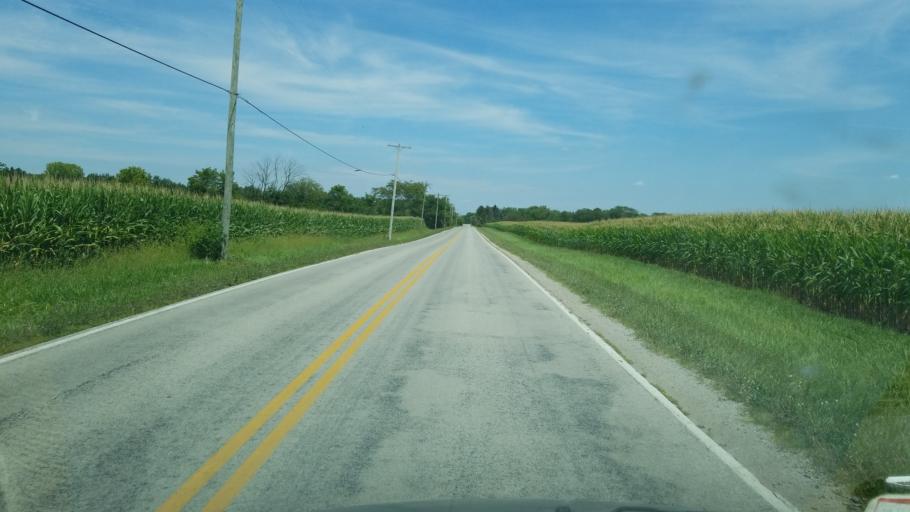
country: US
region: Ohio
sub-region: Madison County
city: West Jefferson
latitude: 39.9224
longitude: -83.2898
